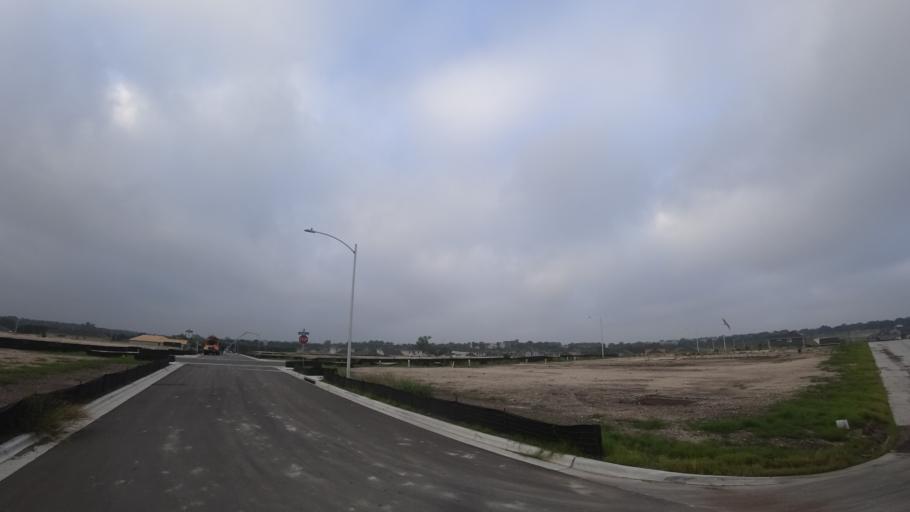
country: US
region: Texas
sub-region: Travis County
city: Wells Branch
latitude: 30.3582
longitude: -97.6634
